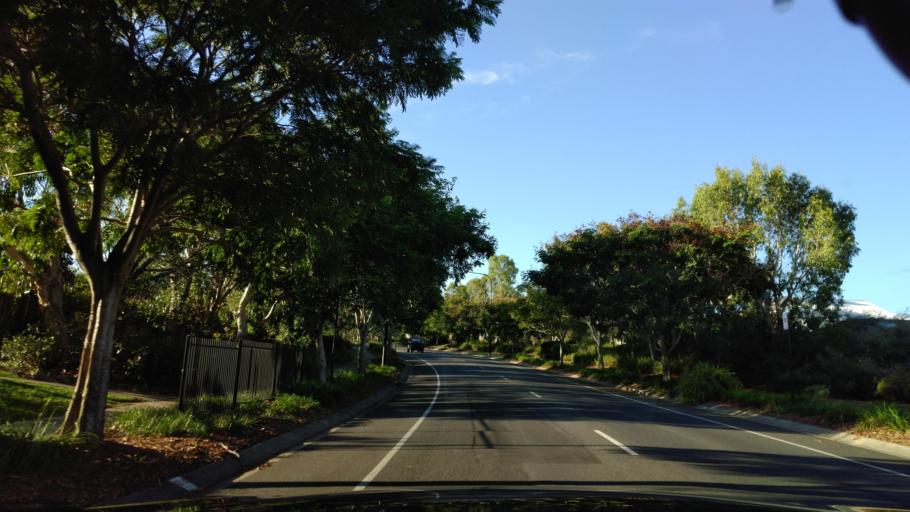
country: AU
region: Queensland
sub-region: Moreton Bay
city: Mango Hill
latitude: -27.2215
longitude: 153.0225
